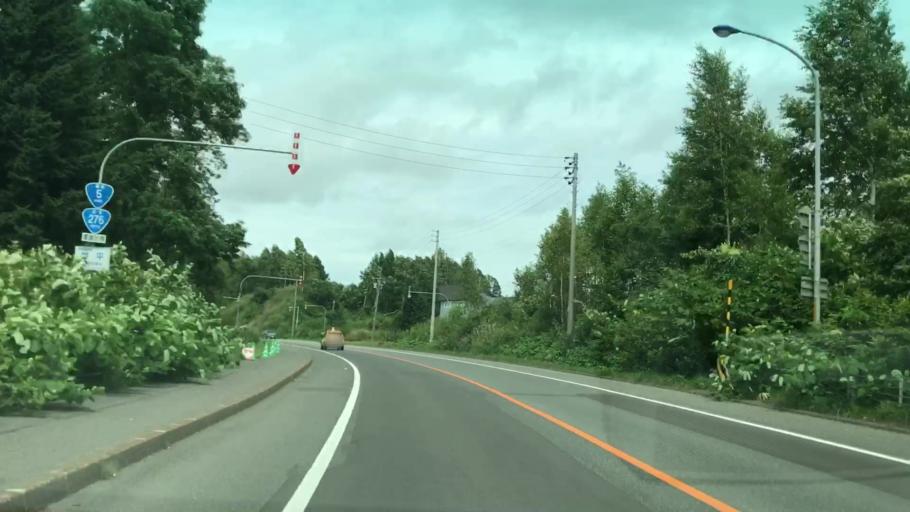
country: JP
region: Hokkaido
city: Niseko Town
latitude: 42.9115
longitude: 140.7532
